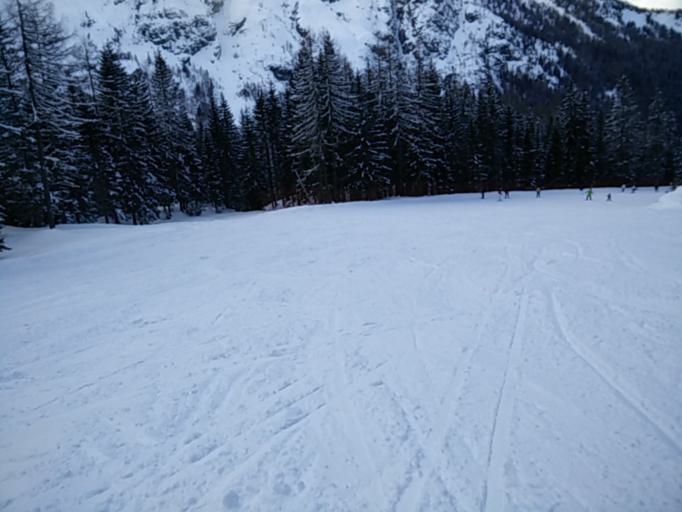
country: IT
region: Veneto
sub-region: Provincia di Belluno
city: Fusine
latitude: 46.3845
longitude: 12.0884
